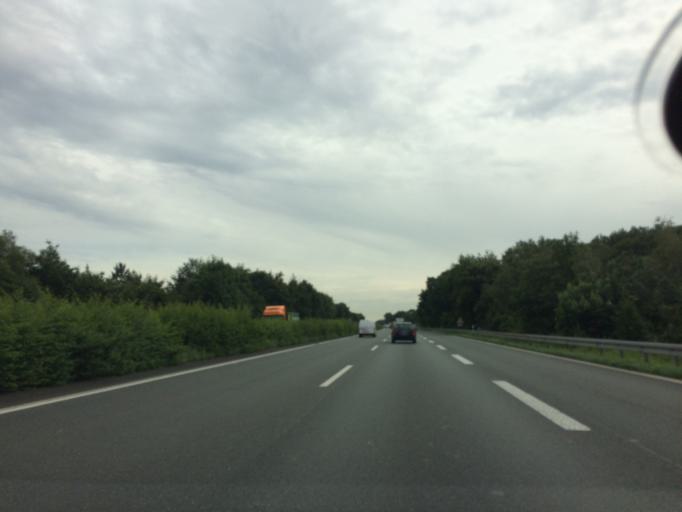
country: DE
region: North Rhine-Westphalia
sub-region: Regierungsbezirk Munster
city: Haltern
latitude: 51.7878
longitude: 7.1787
